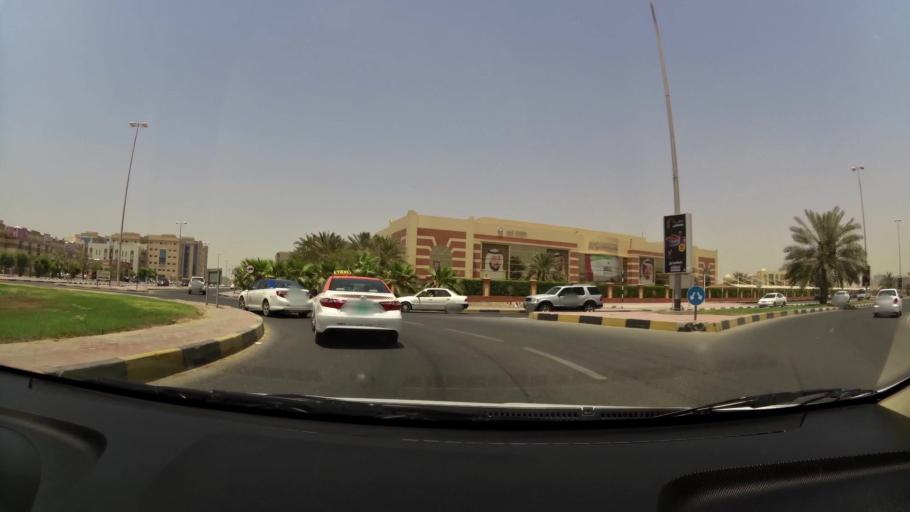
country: AE
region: Ajman
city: Ajman
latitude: 25.4119
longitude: 55.5029
